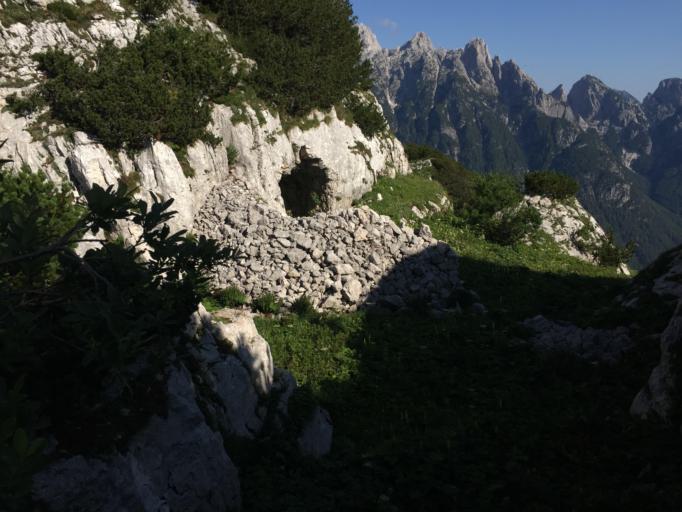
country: SI
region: Bovec
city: Bovec
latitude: 46.3864
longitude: 13.5311
